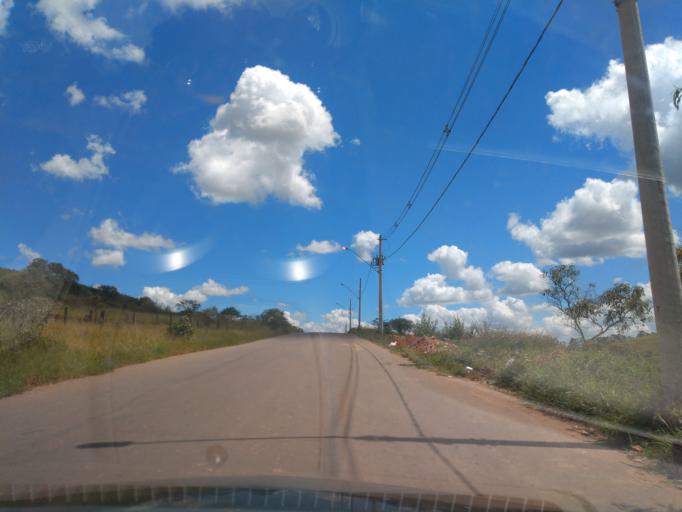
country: BR
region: Minas Gerais
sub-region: Tres Coracoes
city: Tres Coracoes
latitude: -21.6798
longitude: -45.2407
